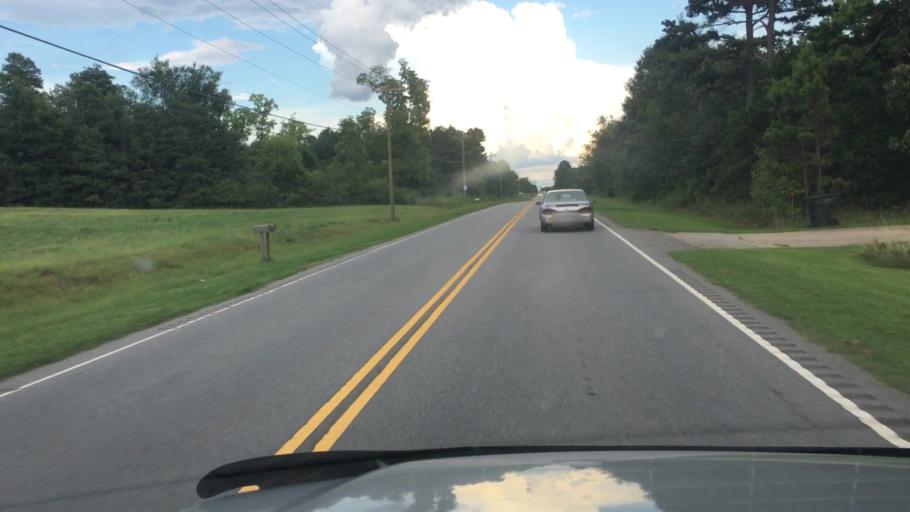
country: US
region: South Carolina
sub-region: Cherokee County
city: Gaffney
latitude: 35.1168
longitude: -81.7105
